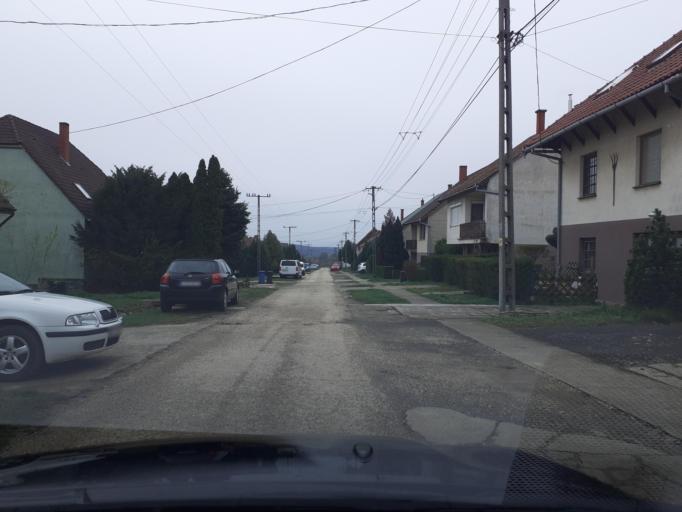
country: HU
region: Tolna
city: Hogyesz
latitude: 46.5008
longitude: 18.4106
